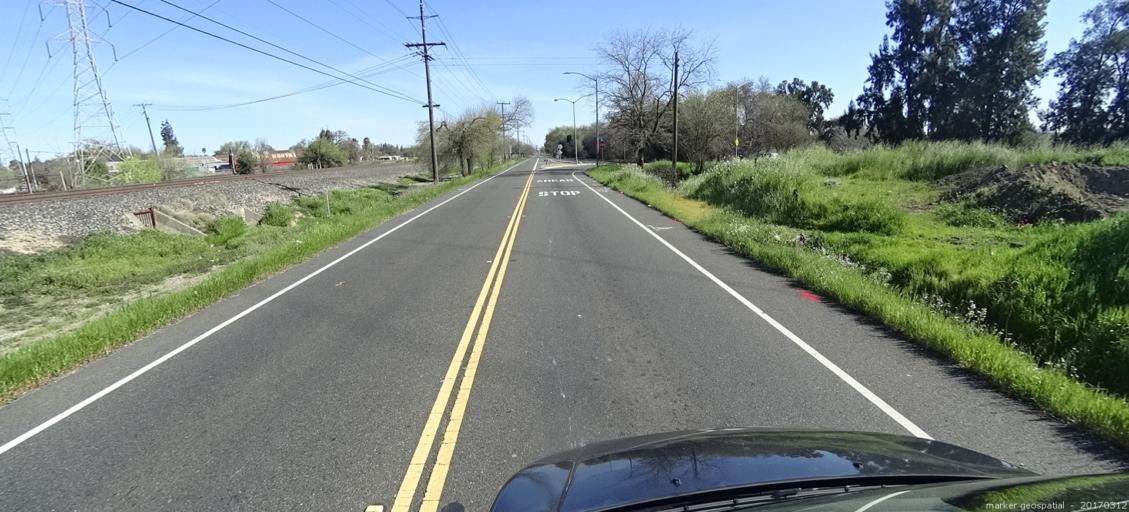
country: US
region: California
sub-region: Sacramento County
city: Arden-Arcade
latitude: 38.6242
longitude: -121.4206
